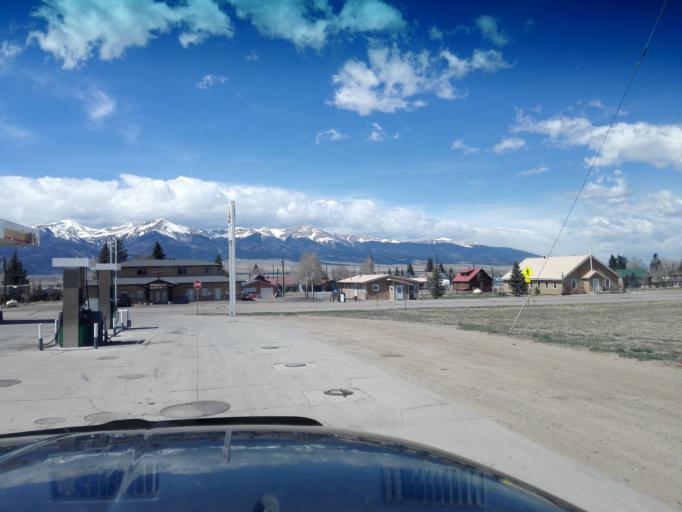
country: US
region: Colorado
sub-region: Custer County
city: Westcliffe
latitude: 38.1315
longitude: -105.4632
